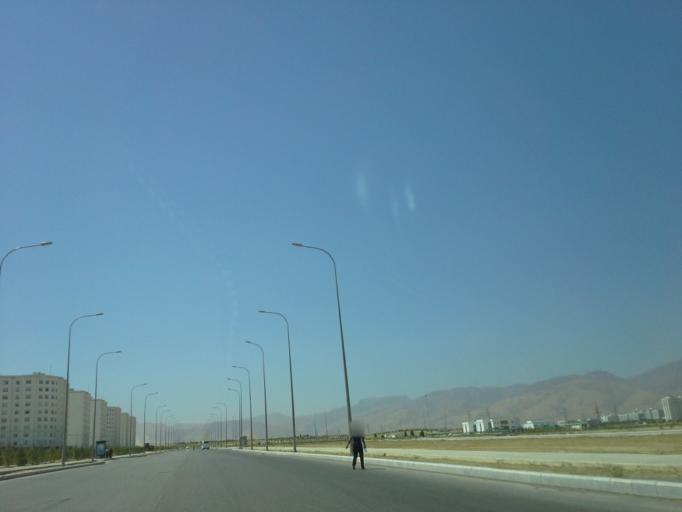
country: TM
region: Ahal
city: Ashgabat
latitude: 37.8926
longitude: 58.4056
